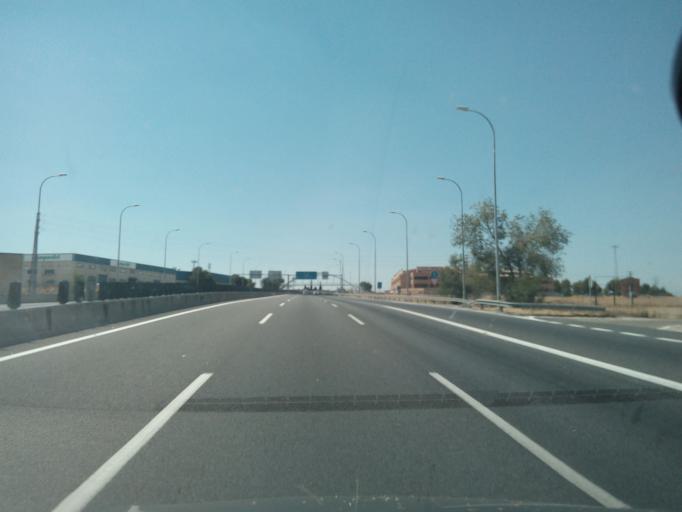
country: ES
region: Castille-La Mancha
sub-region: Province of Toledo
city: Sesena
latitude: 40.1026
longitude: -3.6408
